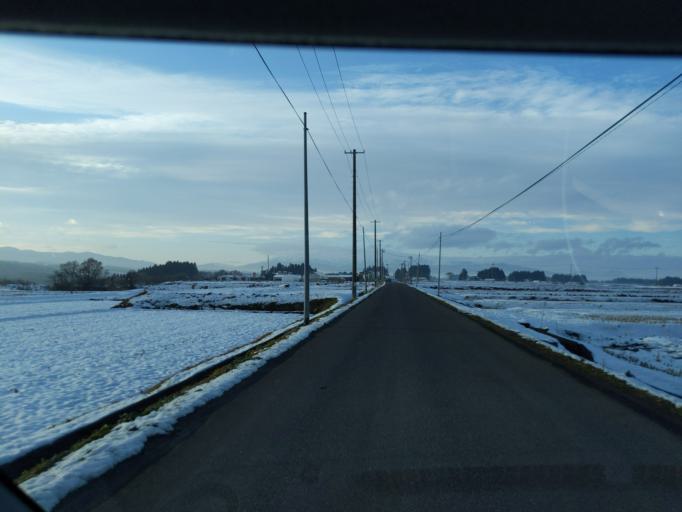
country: JP
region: Iwate
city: Mizusawa
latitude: 39.0509
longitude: 141.1005
